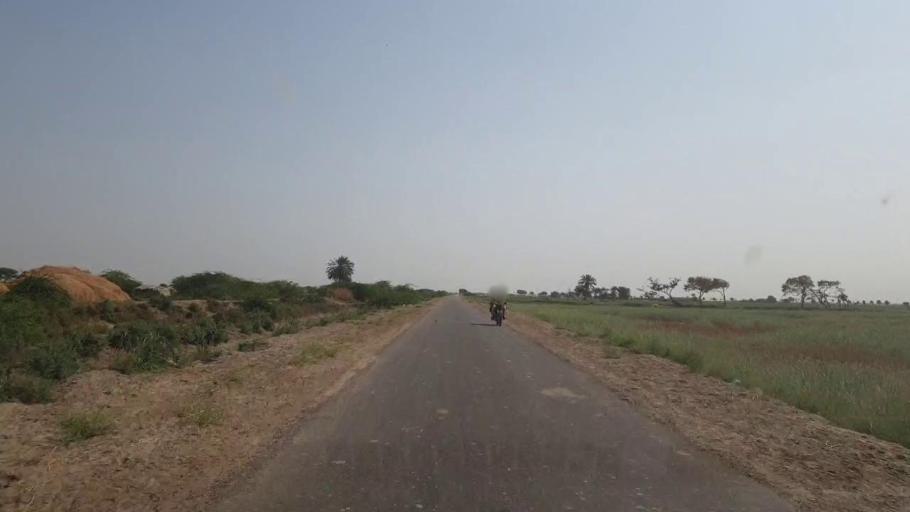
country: PK
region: Sindh
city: Jati
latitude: 24.4562
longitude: 68.5134
